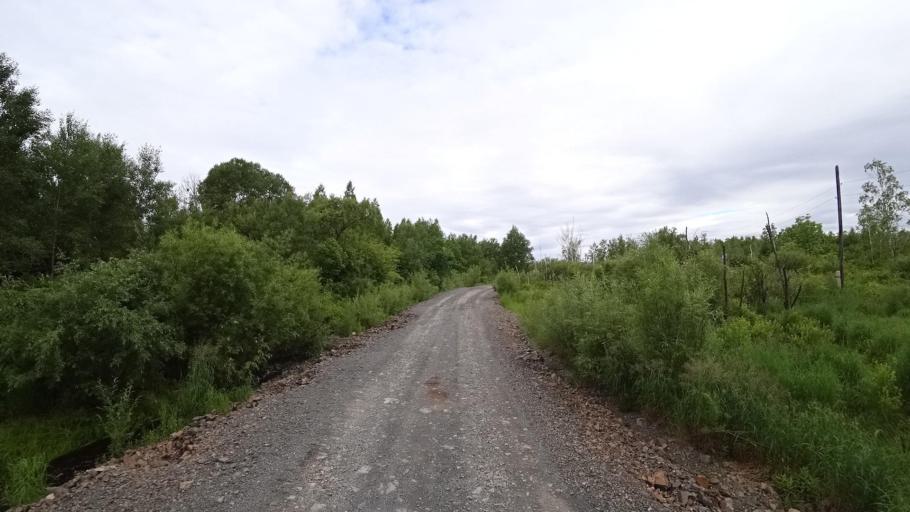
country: RU
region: Khabarovsk Krai
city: Amursk
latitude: 49.8947
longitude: 136.1229
